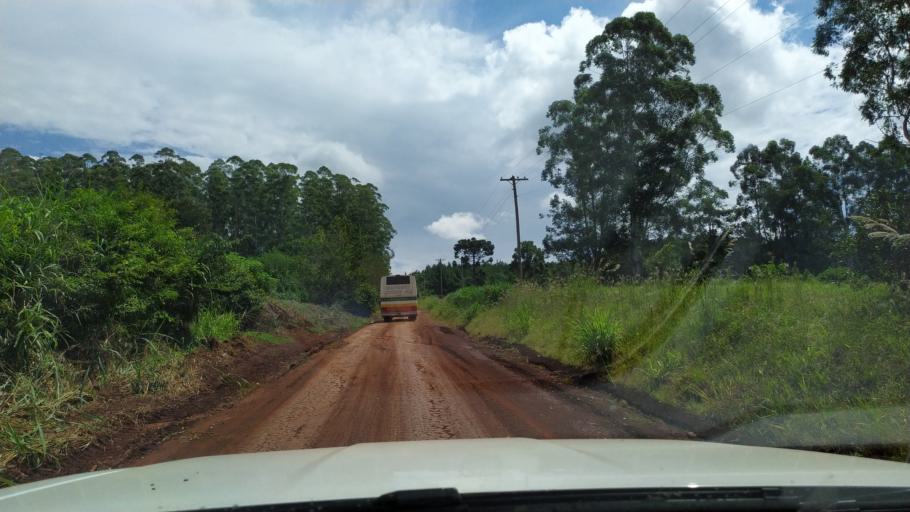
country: AR
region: Misiones
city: Puerto Piray
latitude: -26.5330
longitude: -54.6139
